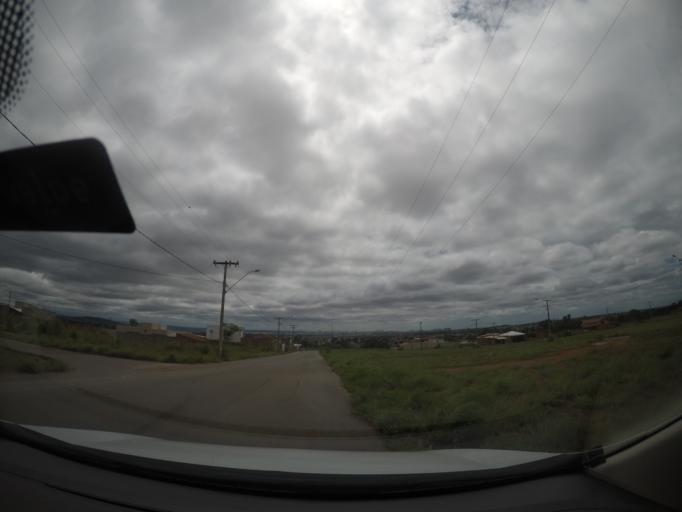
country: BR
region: Goias
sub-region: Trindade
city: Trindade
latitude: -16.7444
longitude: -49.3830
